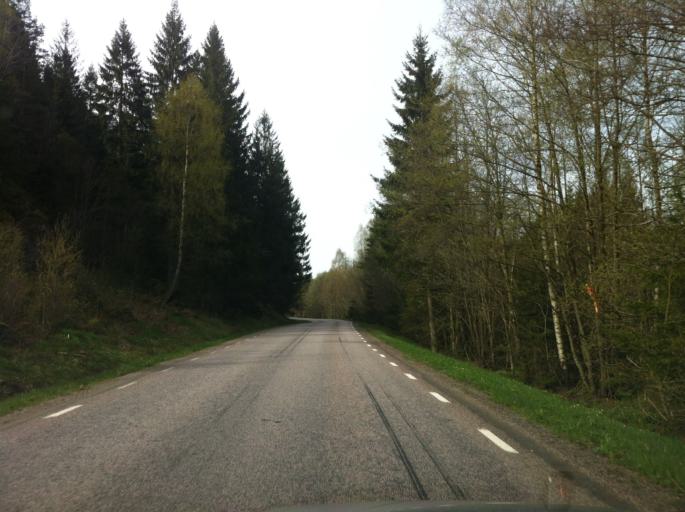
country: SE
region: Vaestra Goetaland
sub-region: Bollebygds Kommun
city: Bollebygd
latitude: 57.5751
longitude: 12.5600
